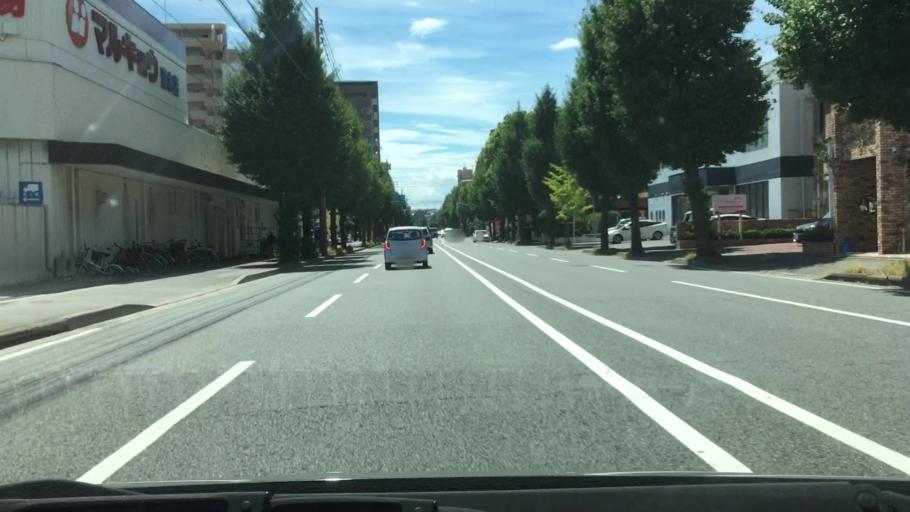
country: JP
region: Fukuoka
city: Fukuoka-shi
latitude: 33.5693
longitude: 130.4252
